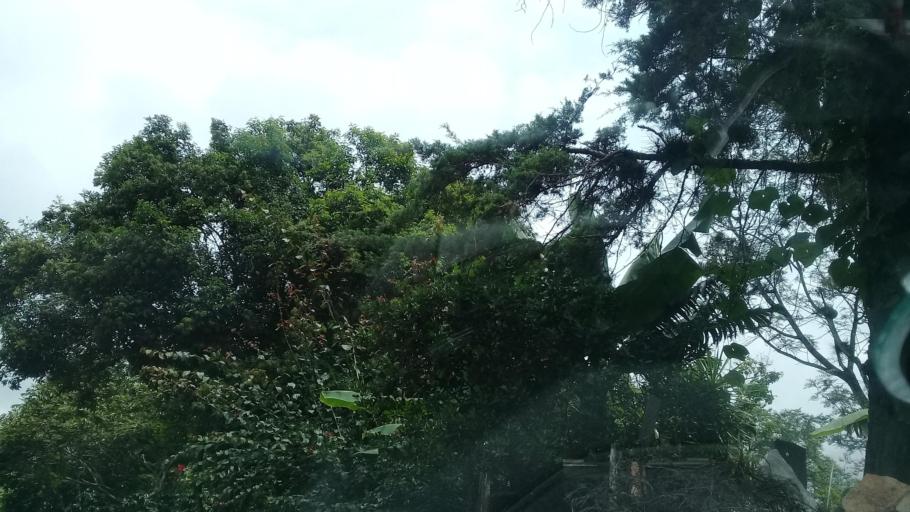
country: MX
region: Veracruz
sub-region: Xalapa
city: Colonia Santa Barbara
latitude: 19.4983
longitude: -96.8734
